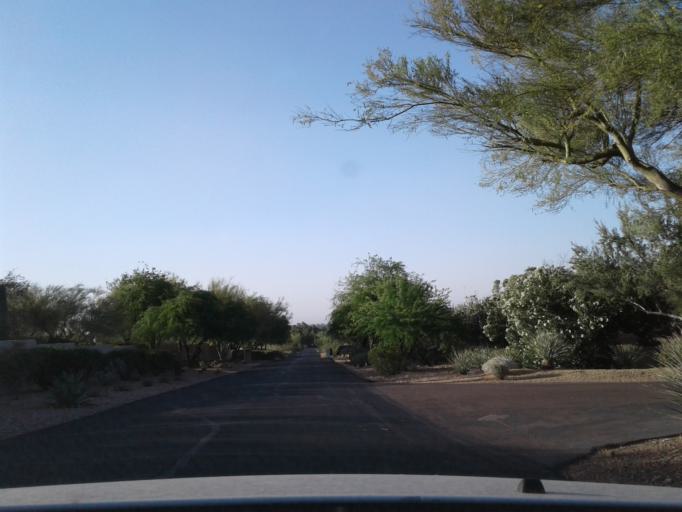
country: US
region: Arizona
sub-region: Maricopa County
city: Paradise Valley
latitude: 33.5553
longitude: -111.9539
